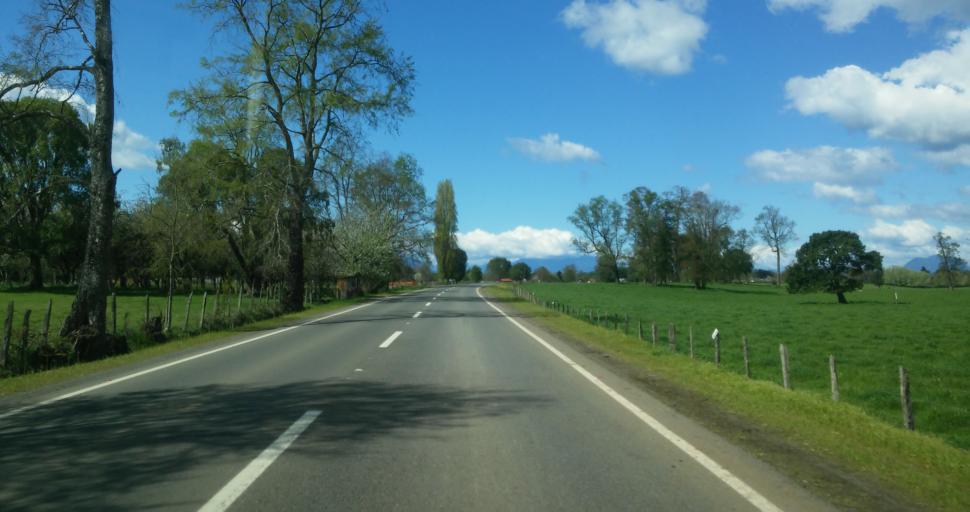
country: CL
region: Los Rios
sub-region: Provincia del Ranco
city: Rio Bueno
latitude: -40.2412
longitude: -72.6074
